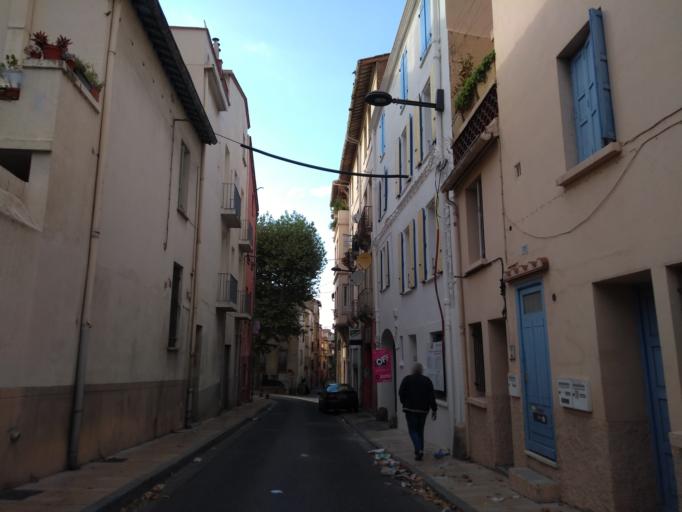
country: FR
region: Languedoc-Roussillon
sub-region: Departement des Pyrenees-Orientales
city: Perpignan
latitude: 42.6944
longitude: 2.8919
